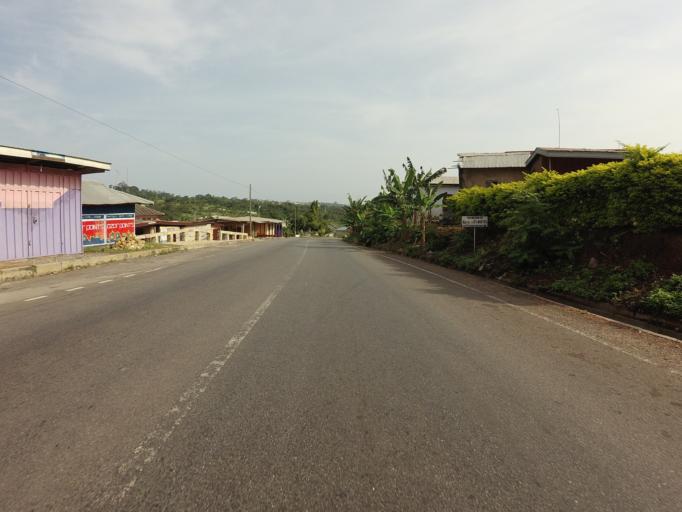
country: GH
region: Eastern
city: Aburi
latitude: 5.8758
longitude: -0.1569
